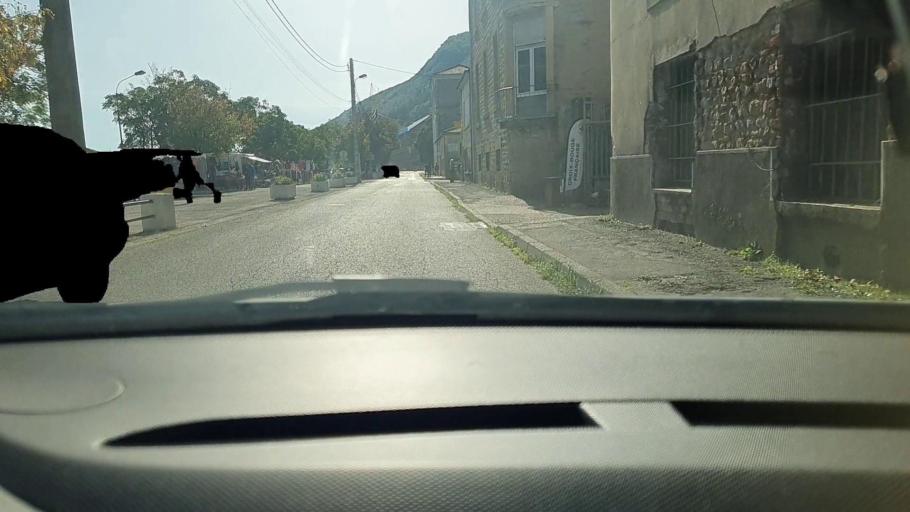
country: FR
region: Languedoc-Roussillon
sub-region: Departement du Gard
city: Besseges
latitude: 44.2927
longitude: 4.0930
